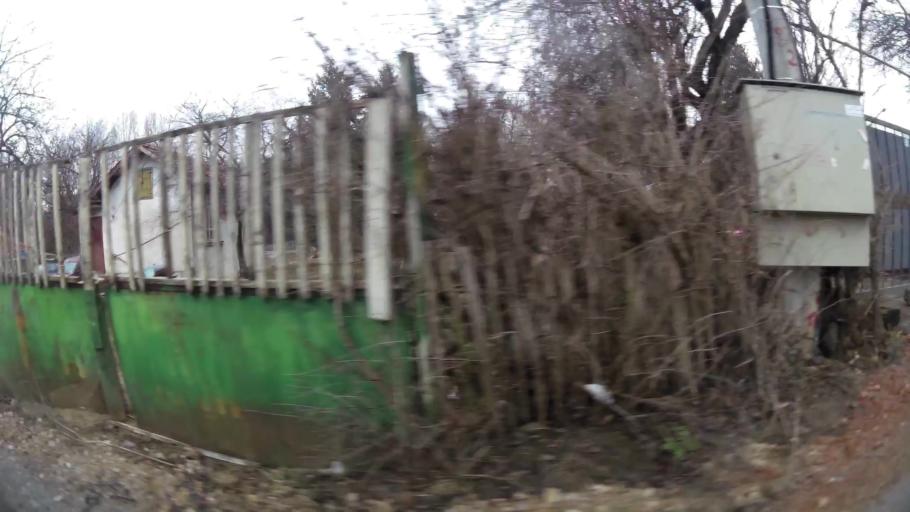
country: BG
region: Sofia-Capital
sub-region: Stolichna Obshtina
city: Sofia
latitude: 42.6178
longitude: 23.3763
